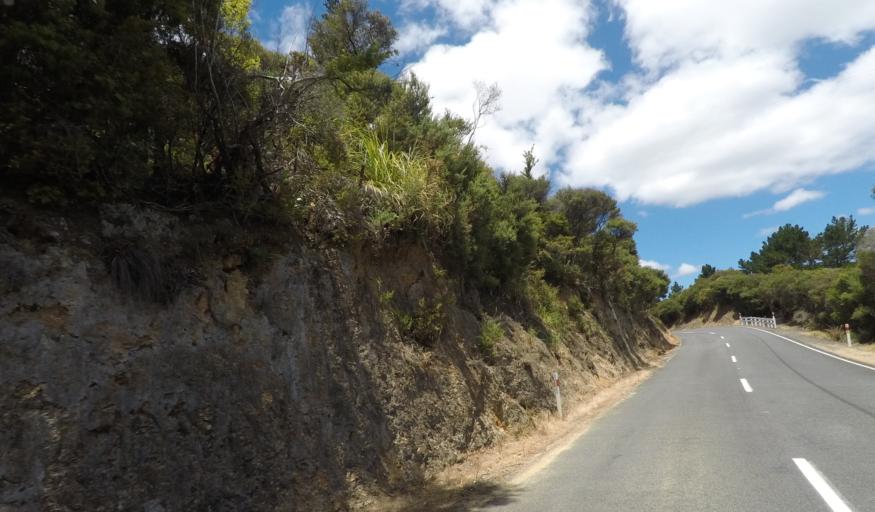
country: NZ
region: Northland
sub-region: Whangarei
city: Ngunguru
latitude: -35.5049
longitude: 174.4342
